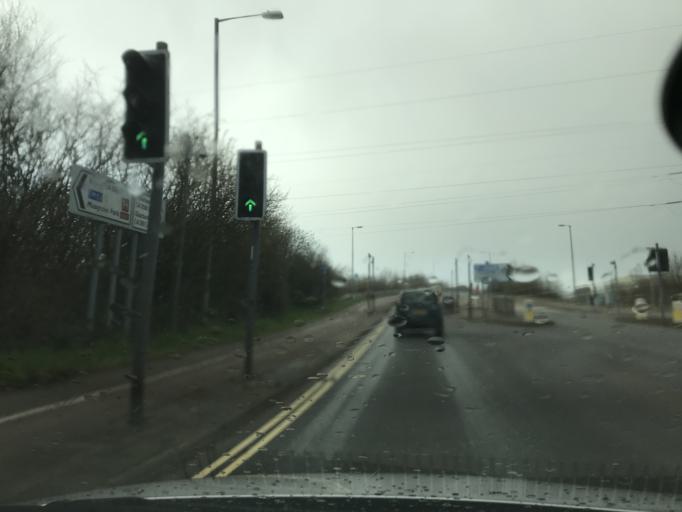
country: GB
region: England
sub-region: Somerset
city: Taunton
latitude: 51.0231
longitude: -3.1326
